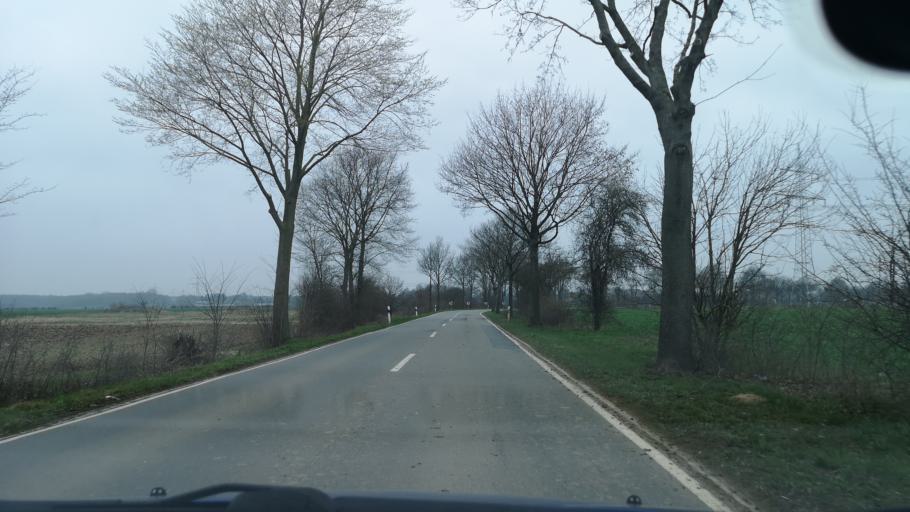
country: DE
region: Lower Saxony
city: Schwarmstedt
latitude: 52.5901
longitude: 9.5747
